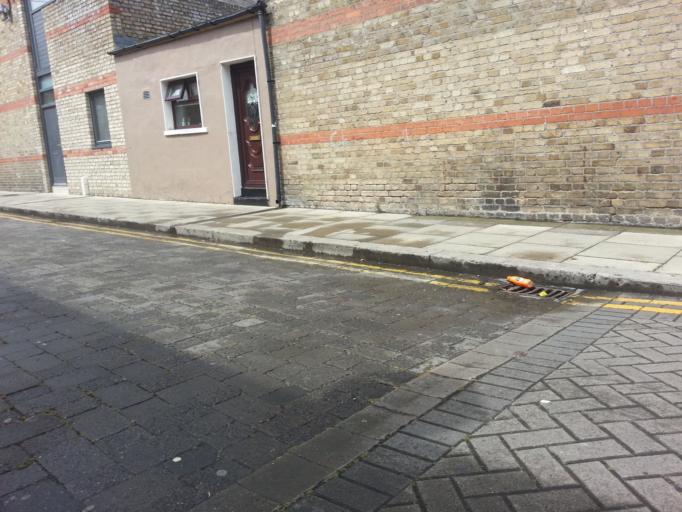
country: IE
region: Leinster
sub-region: Dublin City
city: Dublin
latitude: 53.3463
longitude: -6.2701
